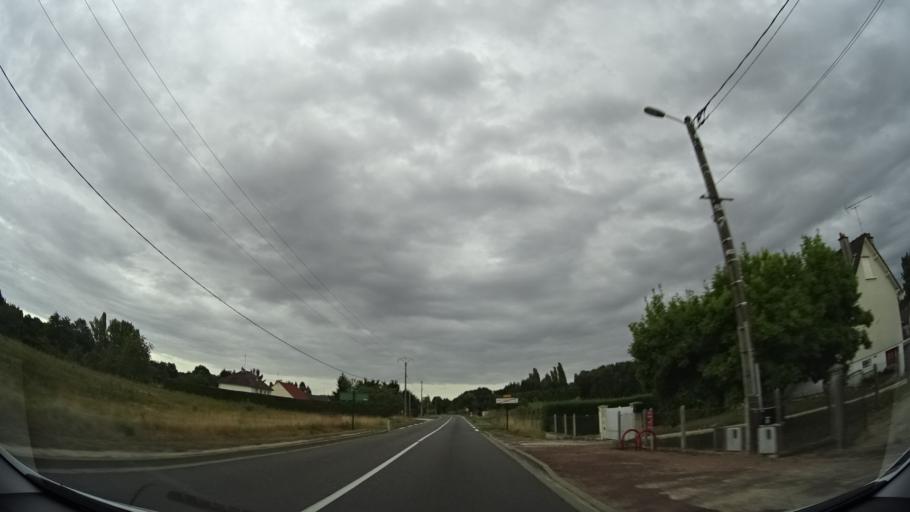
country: FR
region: Centre
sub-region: Departement du Loiret
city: Amilly
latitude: 47.9575
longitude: 2.8065
